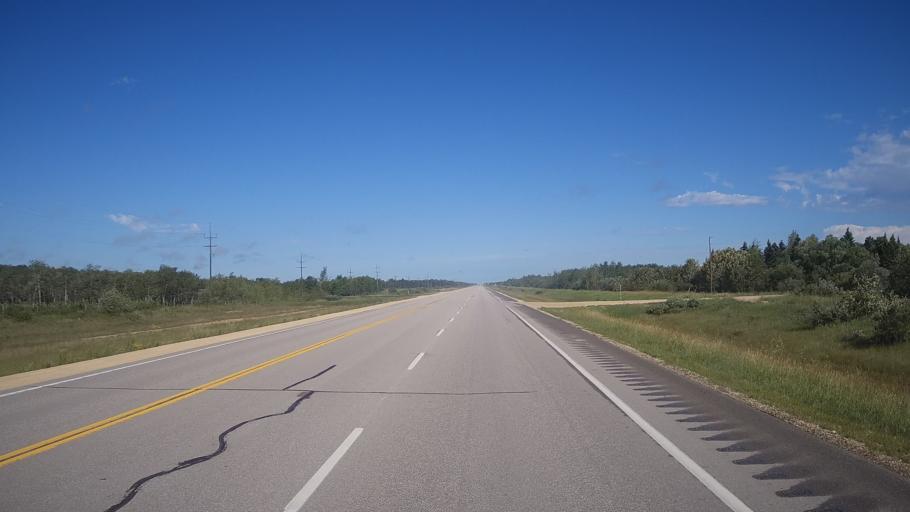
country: CA
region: Manitoba
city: Stonewall
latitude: 50.2250
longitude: -97.6898
